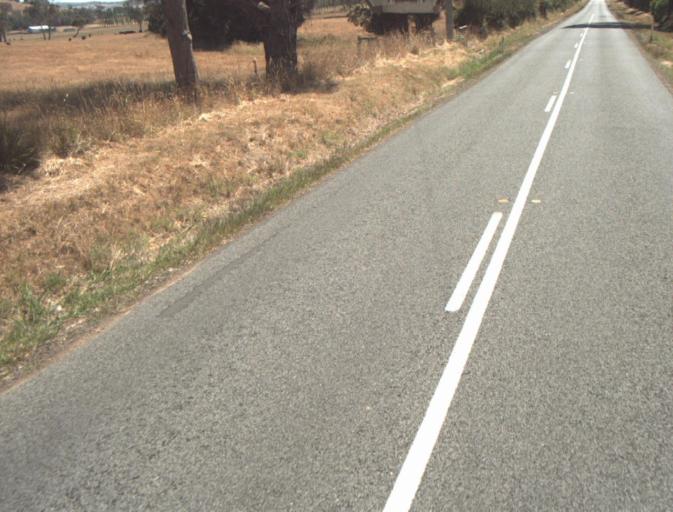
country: AU
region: Tasmania
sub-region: Launceston
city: Mayfield
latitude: -41.2576
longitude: 147.1461
